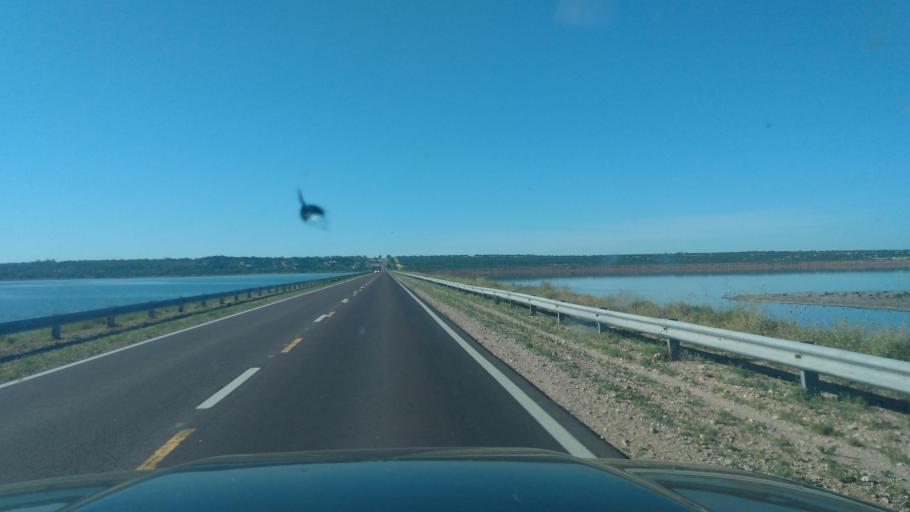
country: AR
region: La Pampa
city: Santa Rosa
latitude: -36.7056
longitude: -64.2831
